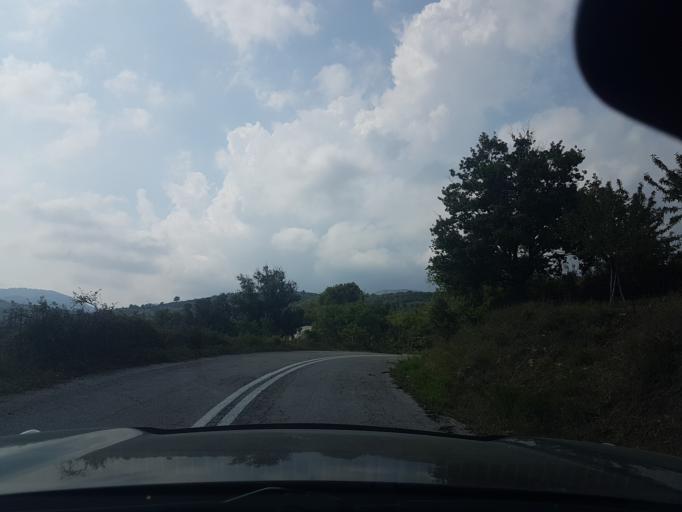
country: GR
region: Central Greece
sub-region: Nomos Evvoias
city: Yimnon
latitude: 38.5364
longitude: 23.9695
